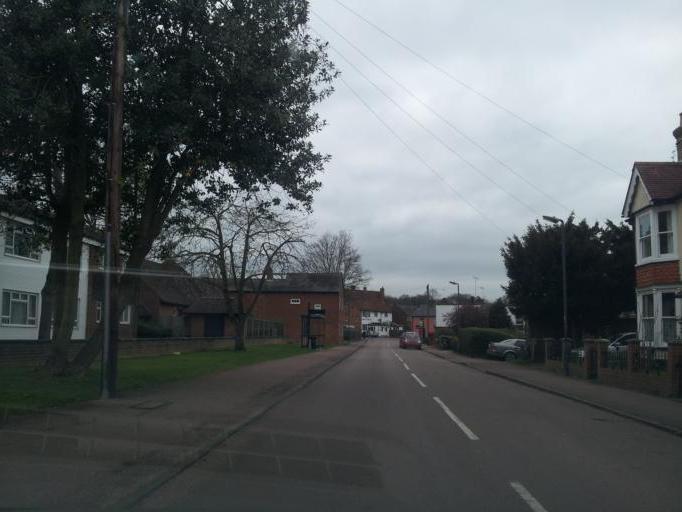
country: GB
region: England
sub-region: Hertfordshire
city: Great Munden
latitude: 51.8899
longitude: 0.0147
